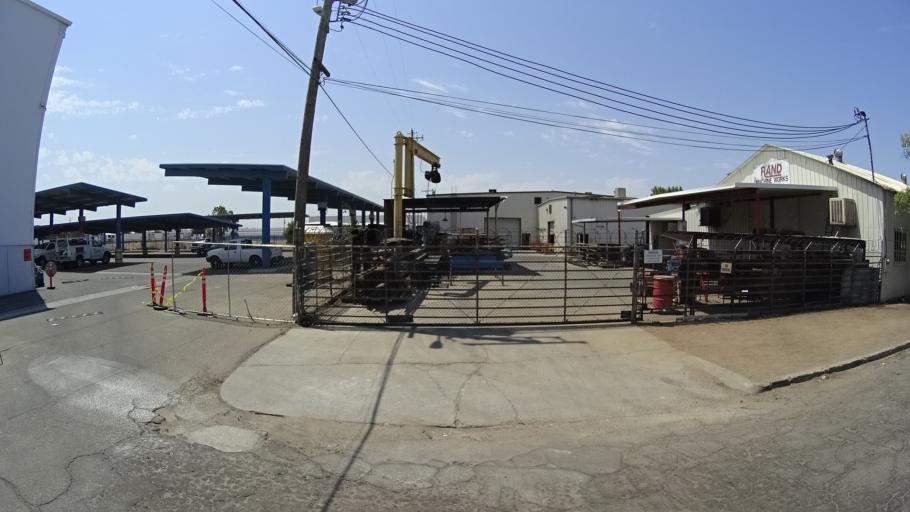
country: US
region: California
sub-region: Fresno County
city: Fresno
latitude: 36.7238
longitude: -119.7757
